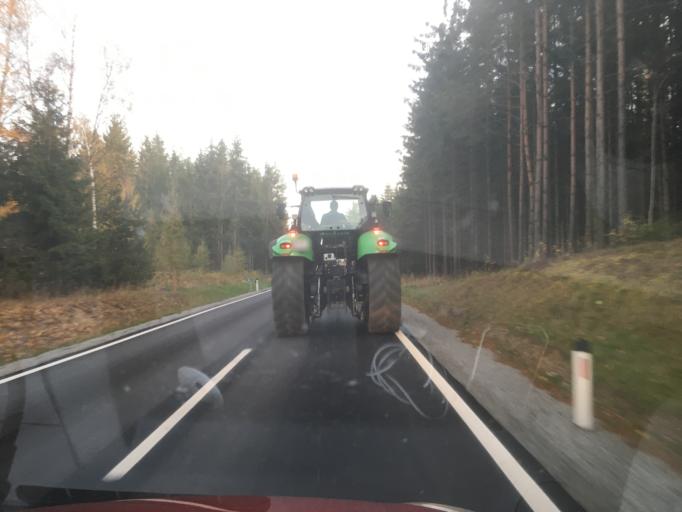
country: AT
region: Lower Austria
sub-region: Politischer Bezirk Zwettl
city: Langschlag
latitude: 48.5709
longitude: 14.9123
